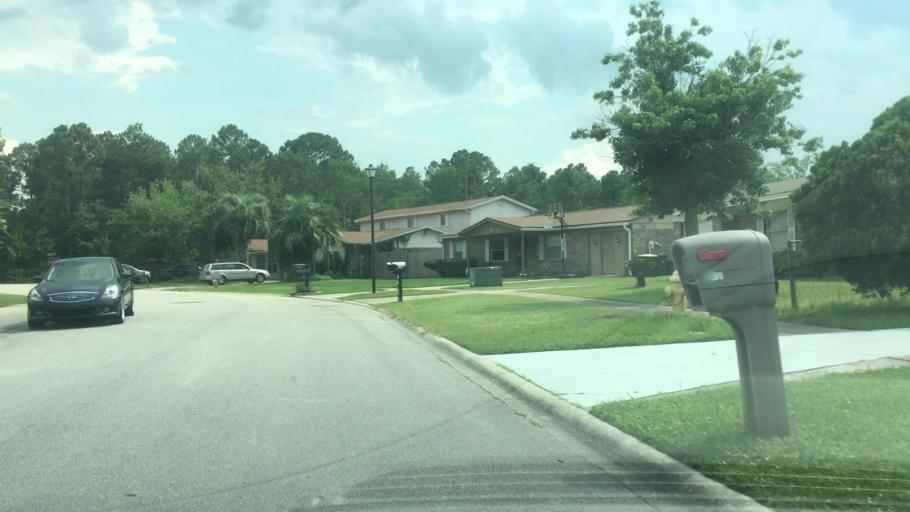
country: US
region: Florida
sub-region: Duval County
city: Neptune Beach
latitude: 30.3028
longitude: -81.5099
